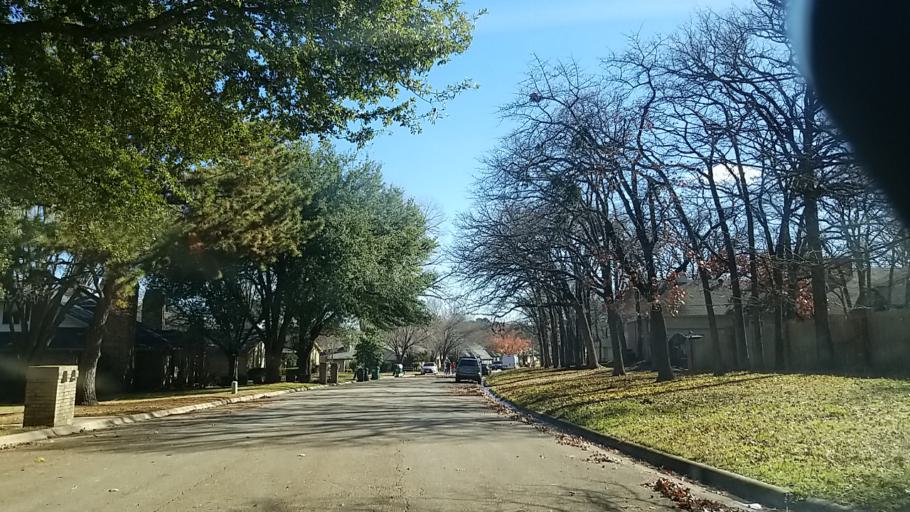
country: US
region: Texas
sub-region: Denton County
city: Denton
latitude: 33.1905
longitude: -97.1170
